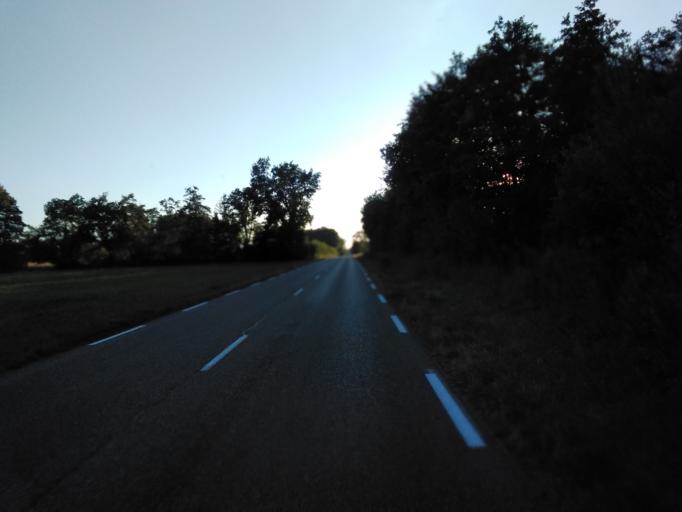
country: FR
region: Rhone-Alpes
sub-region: Departement de l'Isere
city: Chimilin
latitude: 45.5814
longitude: 5.5661
